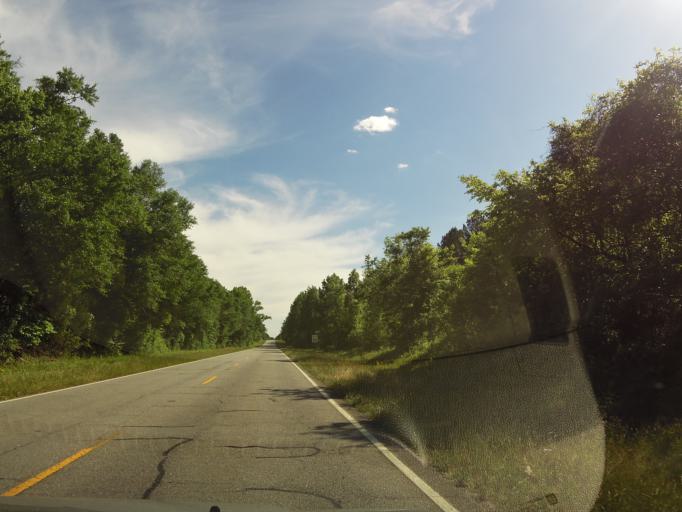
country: US
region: South Carolina
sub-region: Bamberg County
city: Denmark
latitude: 33.1742
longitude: -81.1872
